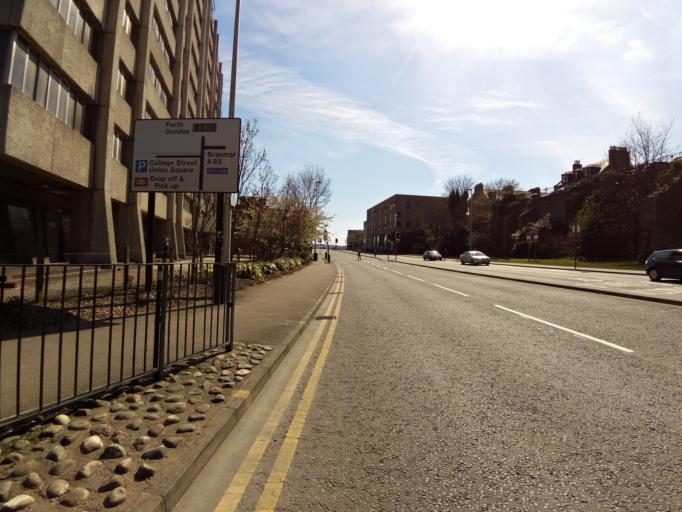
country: GB
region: Scotland
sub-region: Aberdeen City
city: Aberdeen
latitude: 57.1438
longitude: -2.1001
